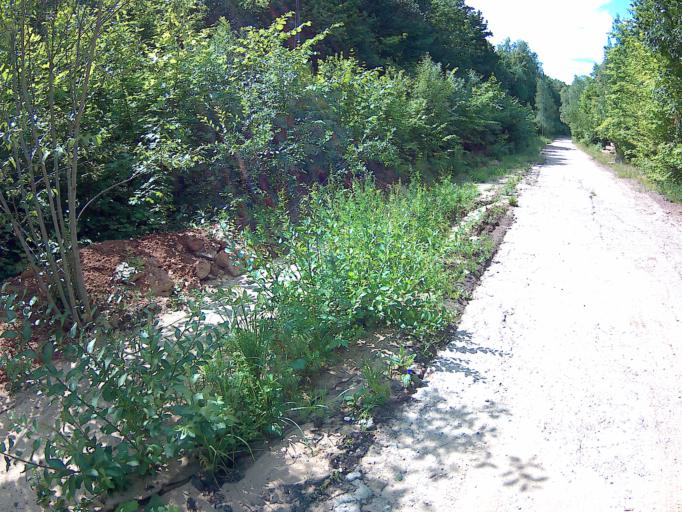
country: RU
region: Nizjnij Novgorod
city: Nizhniy Novgorod
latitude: 56.2247
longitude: 43.9205
